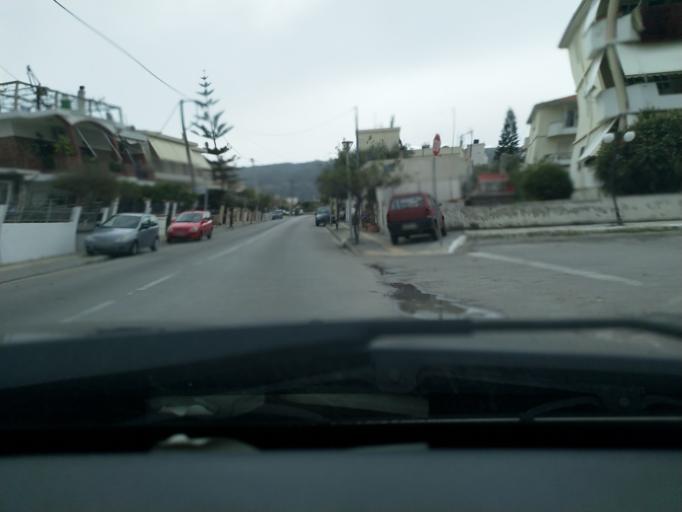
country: GR
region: Crete
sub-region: Nomos Chanias
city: Mournies
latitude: 35.4957
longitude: 24.0224
